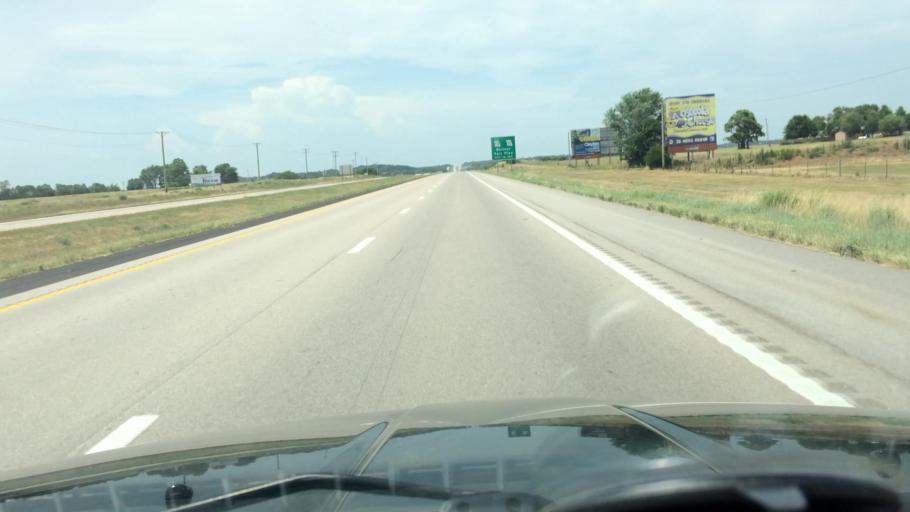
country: US
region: Missouri
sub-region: Polk County
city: Bolivar
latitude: 37.6021
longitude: -93.4392
